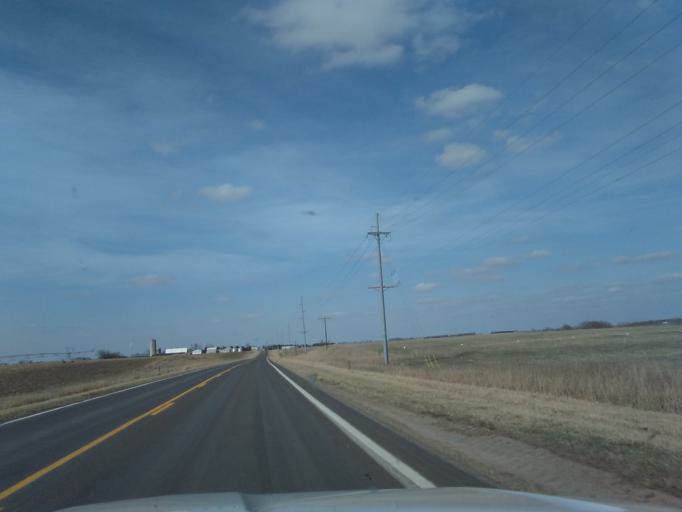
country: US
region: Nebraska
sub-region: Gage County
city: Beatrice
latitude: 40.1757
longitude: -96.9352
